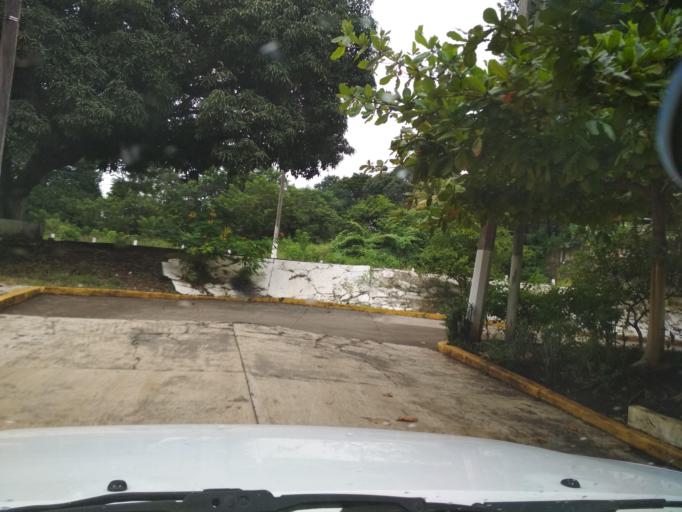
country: MX
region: Veracruz
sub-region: San Andres Tuxtla
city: Los Pinos
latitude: 18.4485
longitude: -95.2294
